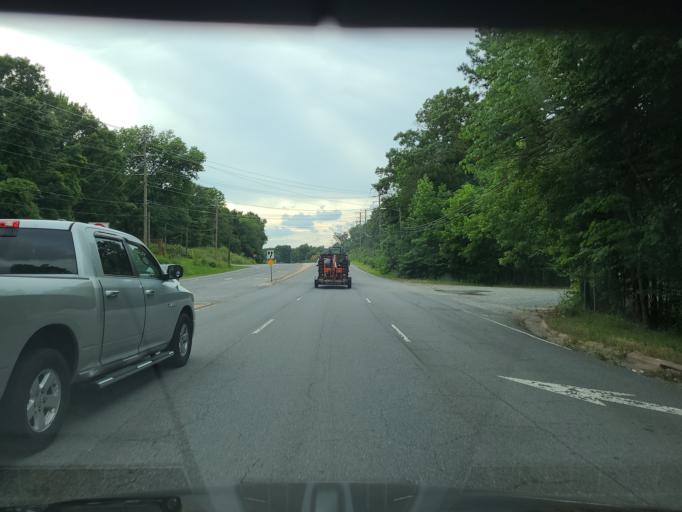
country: US
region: North Carolina
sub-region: Gaston County
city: Belmont
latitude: 35.2371
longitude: -80.9580
